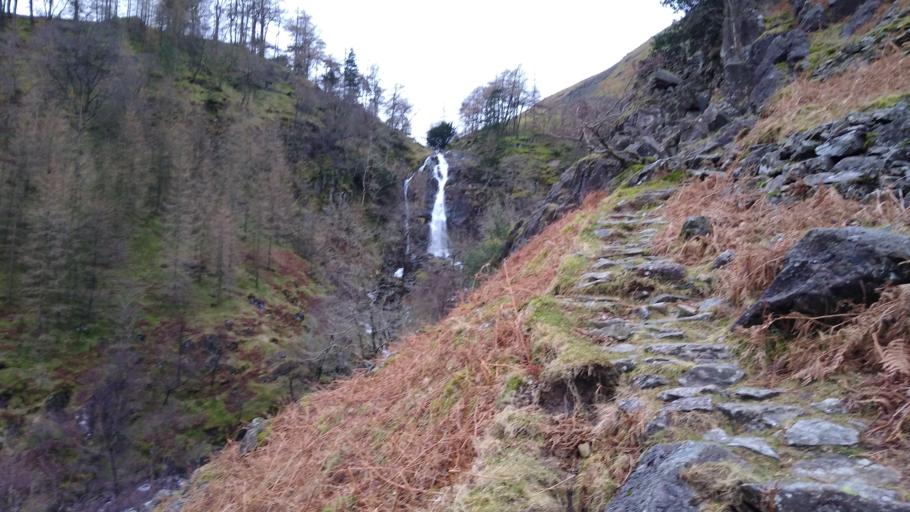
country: GB
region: England
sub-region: Cumbria
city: Keswick
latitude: 54.4888
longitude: -3.1886
